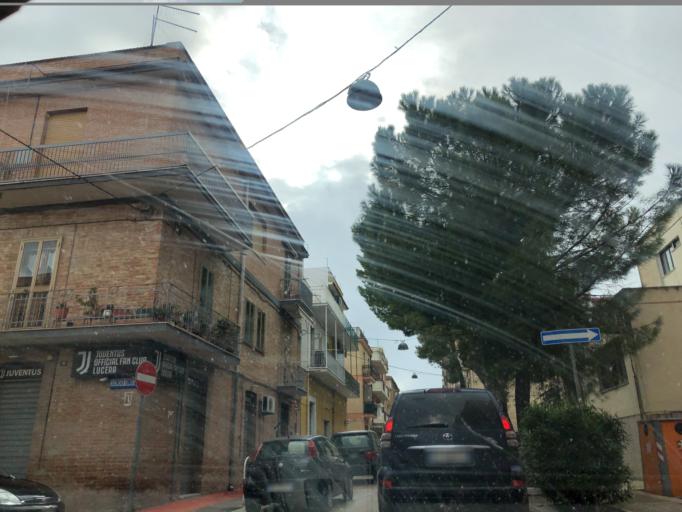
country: IT
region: Apulia
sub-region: Provincia di Foggia
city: Lucera
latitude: 41.5086
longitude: 15.3300
